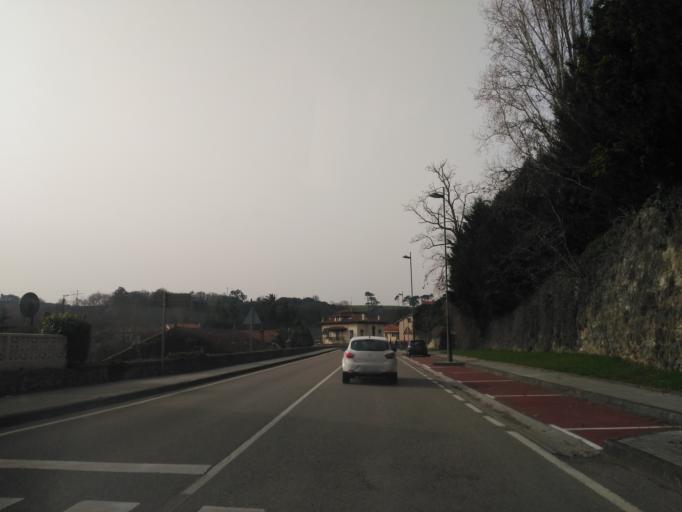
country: ES
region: Cantabria
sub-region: Provincia de Cantabria
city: Comillas
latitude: 43.3873
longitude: -4.2943
